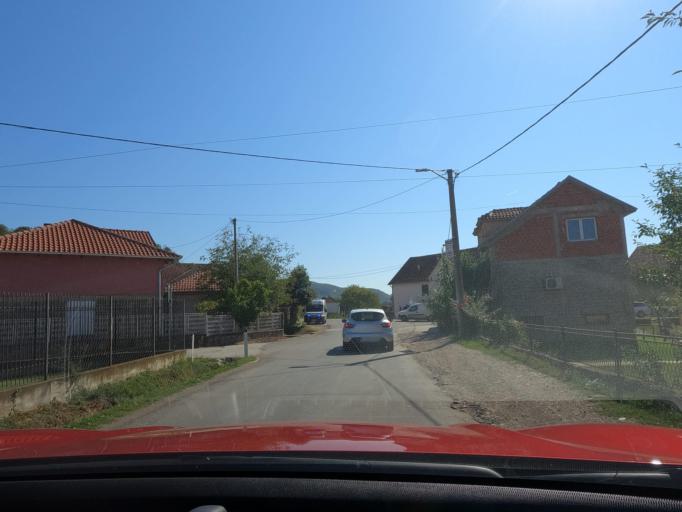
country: RS
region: Central Serbia
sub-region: Raski Okrug
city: Kraljevo
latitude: 43.7456
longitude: 20.7208
